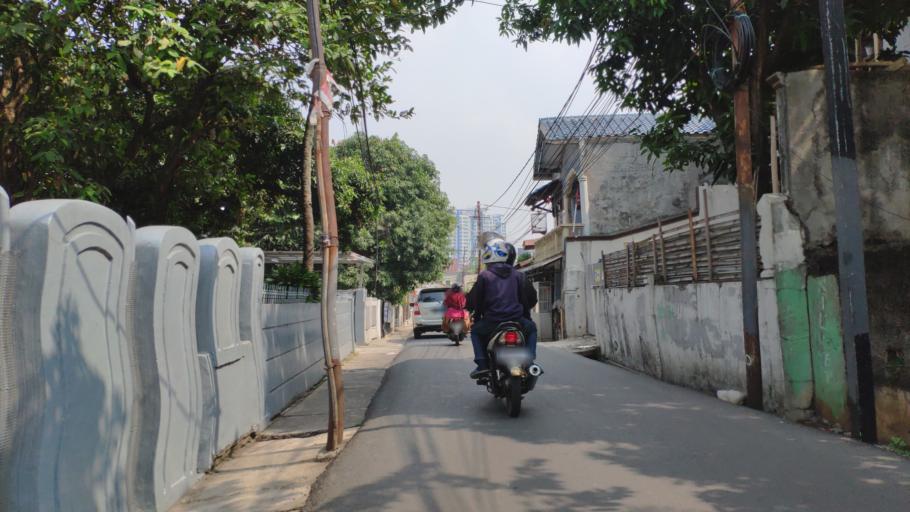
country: ID
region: Banten
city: South Tangerang
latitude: -6.2883
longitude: 106.7907
